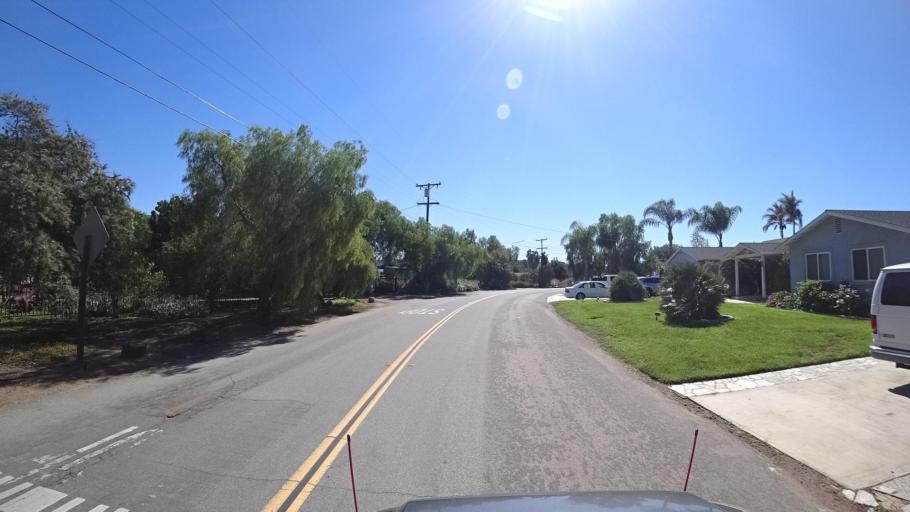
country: US
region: California
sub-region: San Diego County
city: Bonita
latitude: 32.6582
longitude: -117.0485
